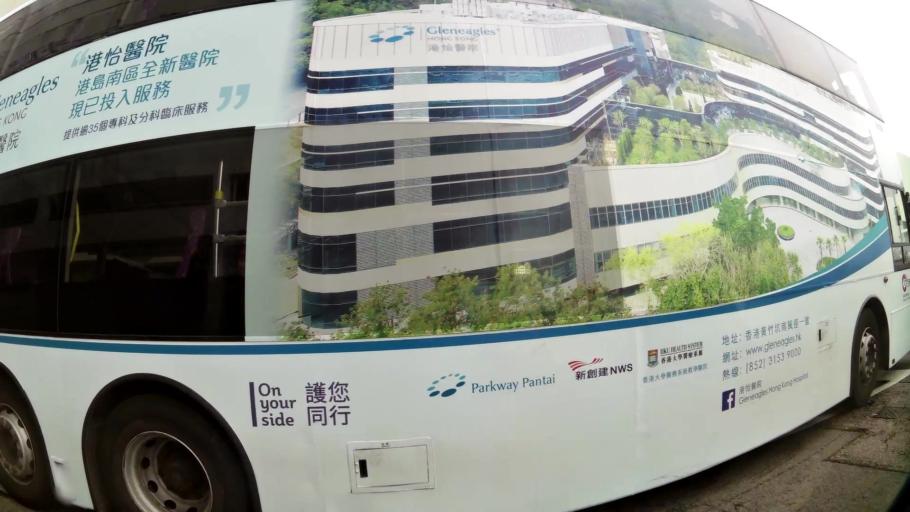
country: HK
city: Sok Kwu Wan
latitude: 22.2375
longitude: 114.1535
